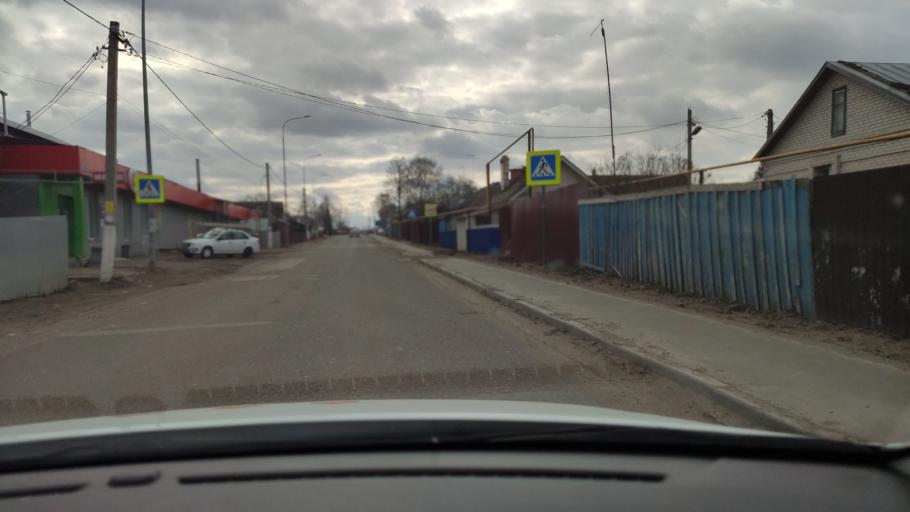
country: RU
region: Tatarstan
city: Vysokaya Gora
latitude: 56.1236
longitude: 49.1963
